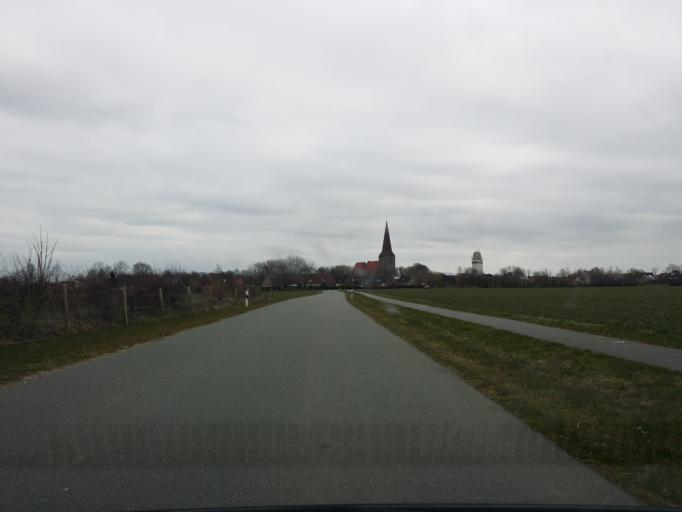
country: DE
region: Schleswig-Holstein
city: Grossenbrode
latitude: 54.4822
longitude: 11.0599
